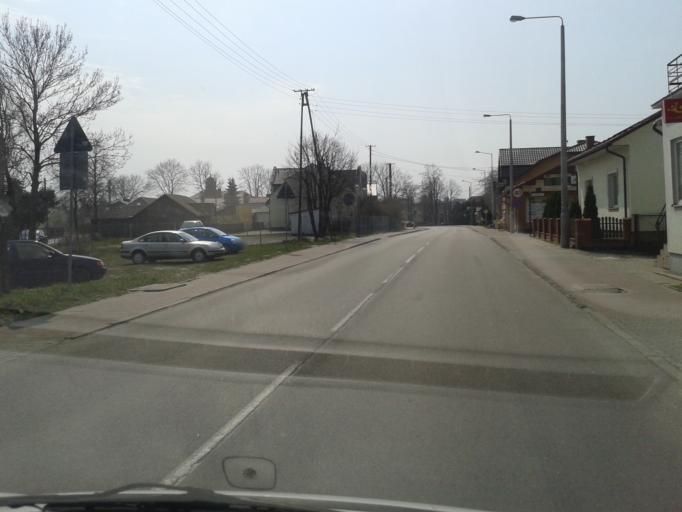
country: PL
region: Subcarpathian Voivodeship
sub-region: Powiat lubaczowski
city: Narol
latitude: 50.3508
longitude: 23.3269
